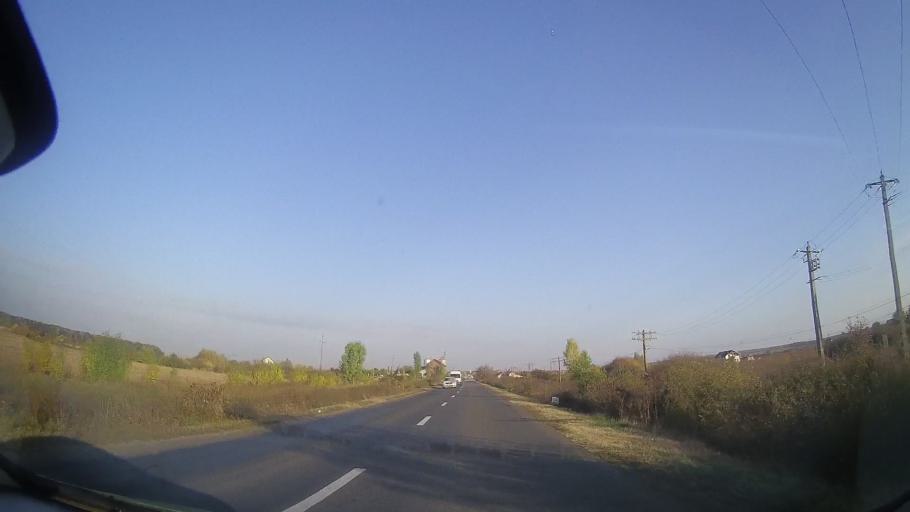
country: RO
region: Timis
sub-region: Comuna Pischia
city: Pischia
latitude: 45.8927
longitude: 21.3465
